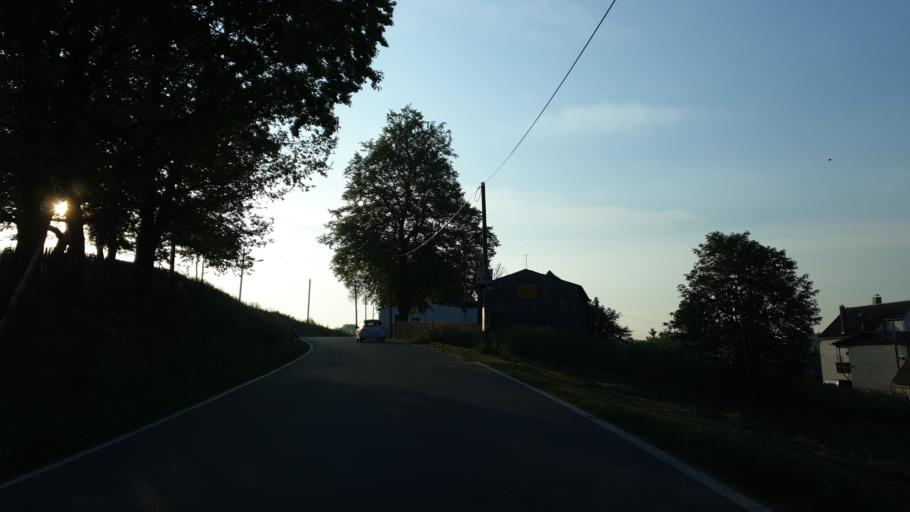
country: DE
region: Saxony
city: Bernsdorf
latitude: 50.7849
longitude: 12.6650
